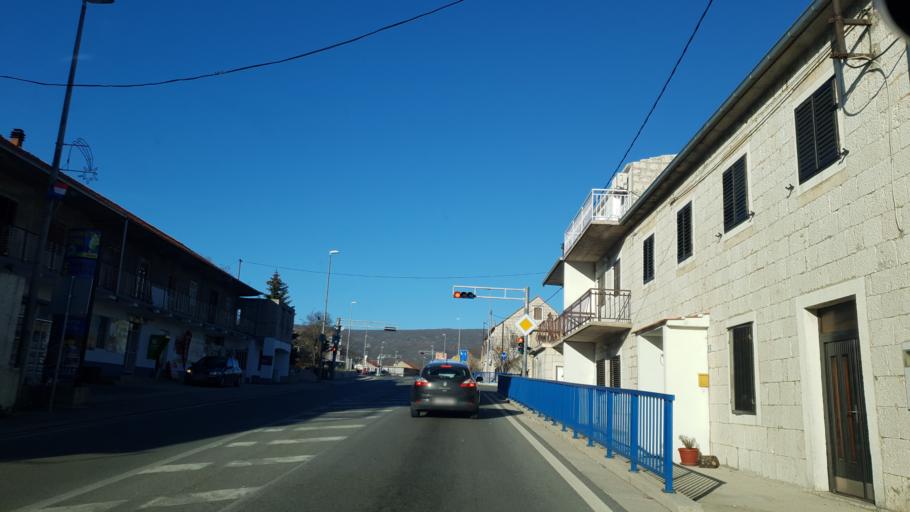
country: HR
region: Splitsko-Dalmatinska
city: Dugopolje
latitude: 43.6337
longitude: 16.5955
